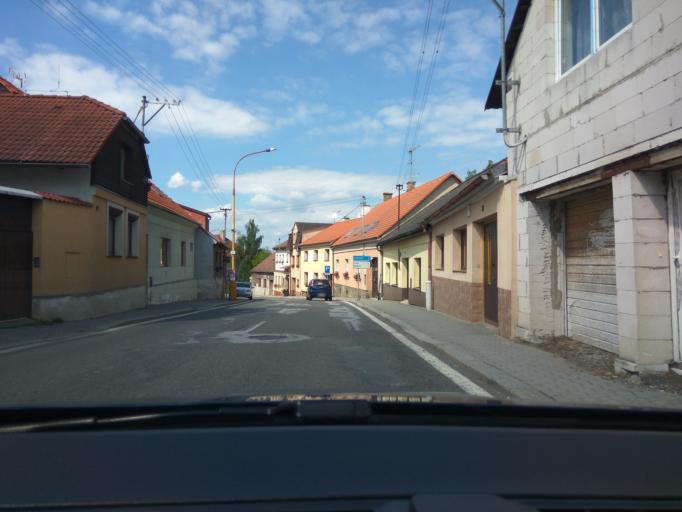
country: CZ
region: Jihocesky
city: Milevsko
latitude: 49.4463
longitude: 14.3603
